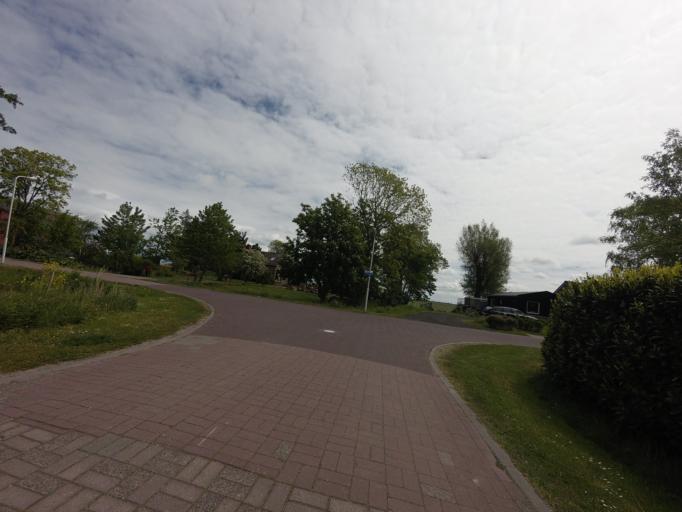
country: NL
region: Friesland
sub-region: Gemeente Gaasterlan-Sleat
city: Balk
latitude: 52.9239
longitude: 5.5393
